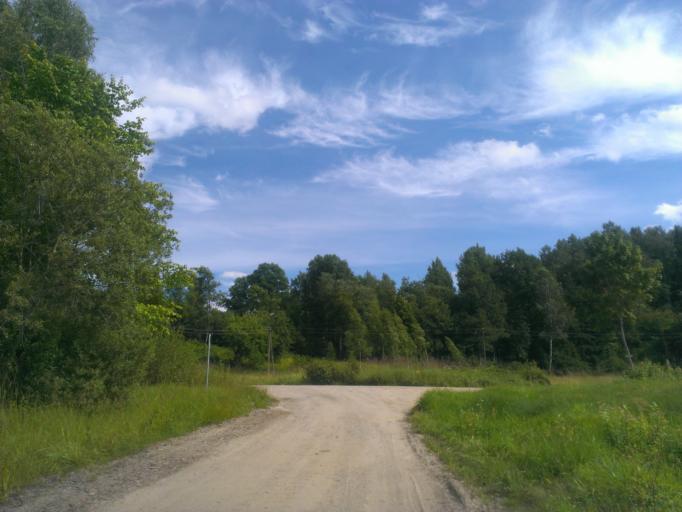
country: LV
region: Ligatne
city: Ligatne
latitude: 57.2115
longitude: 25.0104
